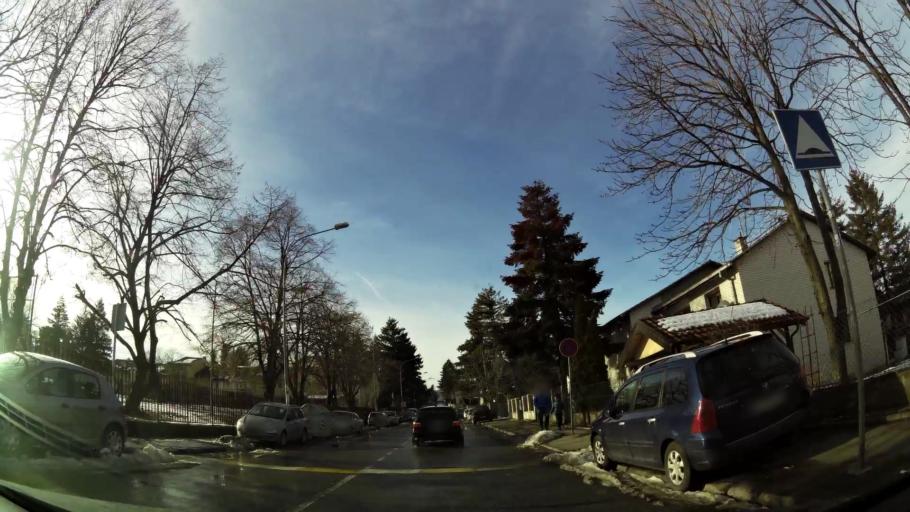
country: RS
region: Central Serbia
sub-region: Belgrade
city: Rakovica
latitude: 44.7207
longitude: 20.4230
